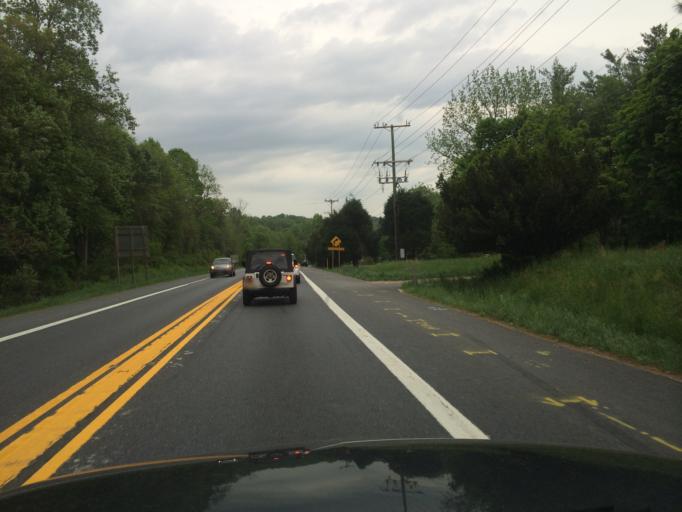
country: US
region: Maryland
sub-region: Carroll County
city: Sykesville
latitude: 39.3559
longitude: -76.9678
